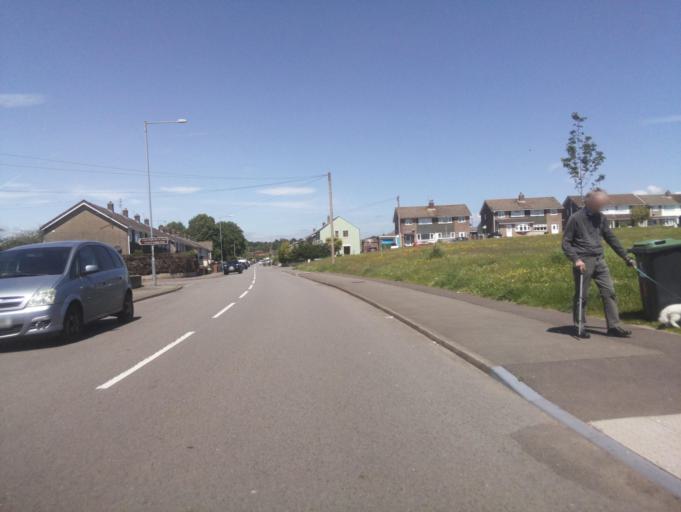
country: GB
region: Wales
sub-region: Monmouthshire
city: Caldicot
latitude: 51.5875
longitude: -2.7635
